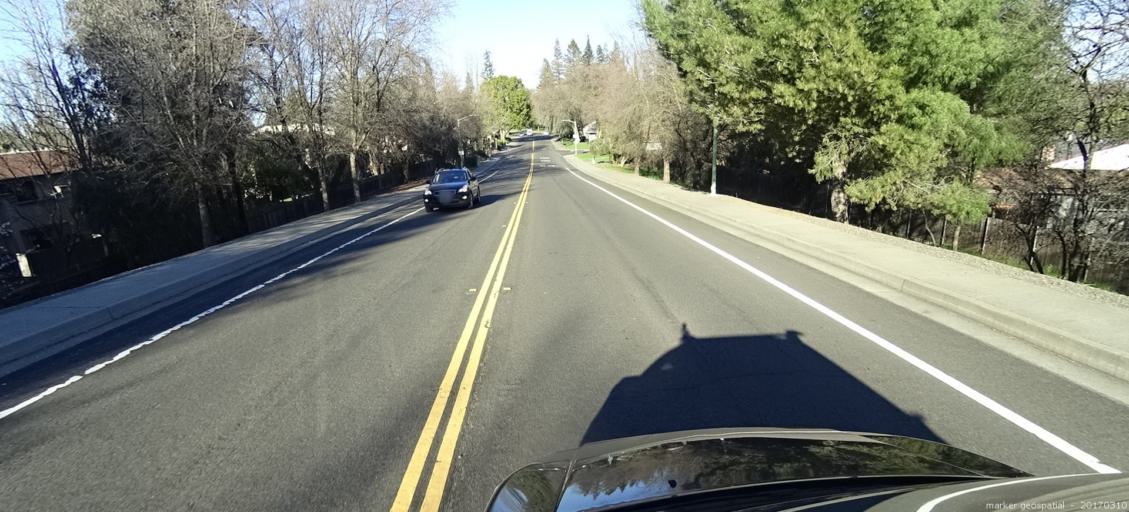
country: US
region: California
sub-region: Sacramento County
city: Parkway
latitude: 38.5097
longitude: -121.5213
